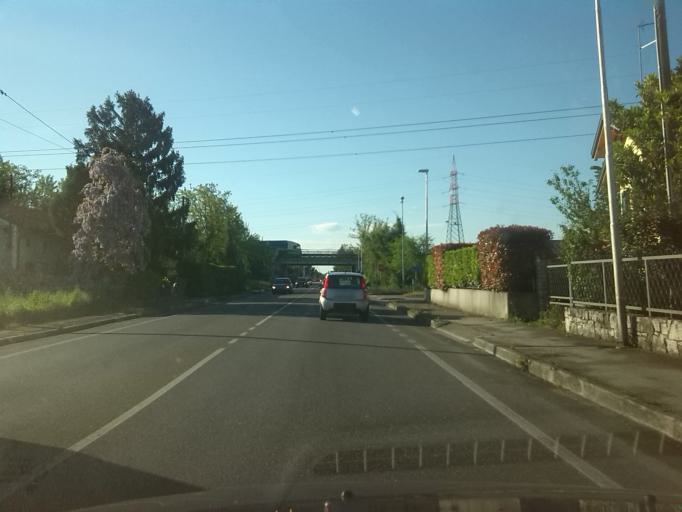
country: IT
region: Friuli Venezia Giulia
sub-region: Provincia di Gorizia
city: Ronchi dei Legionari
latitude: 45.8438
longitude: 13.4905
